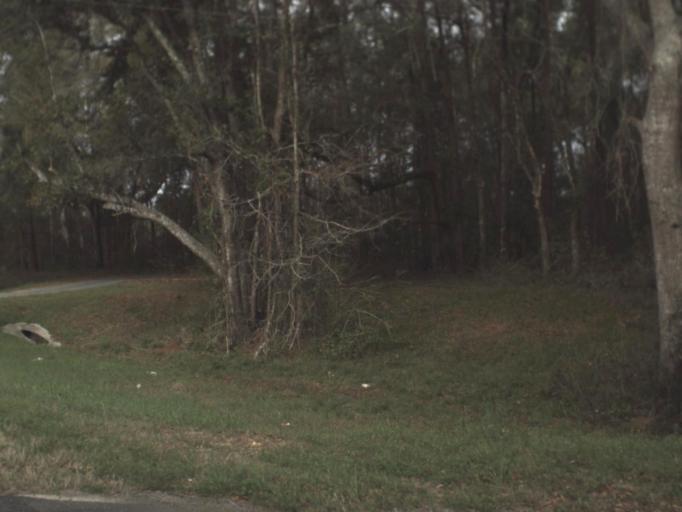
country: US
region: Florida
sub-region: Jefferson County
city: Monticello
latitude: 30.5202
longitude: -84.0364
